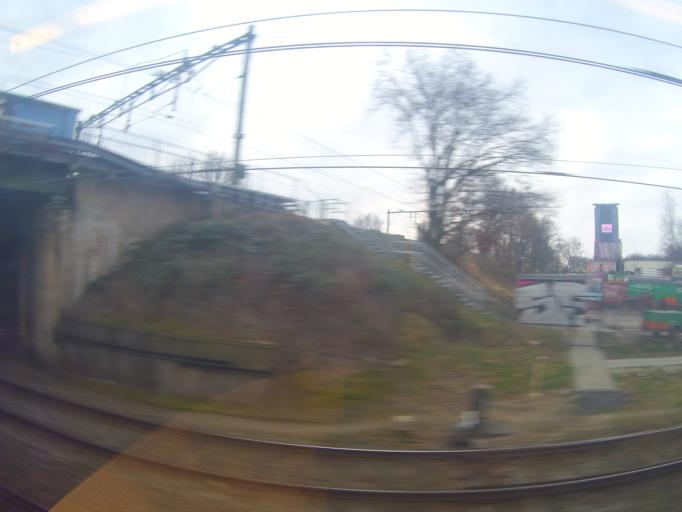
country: NL
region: South Holland
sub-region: Gemeente Leidschendam-Voorburg
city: Voorburg
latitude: 52.0751
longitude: 4.3342
